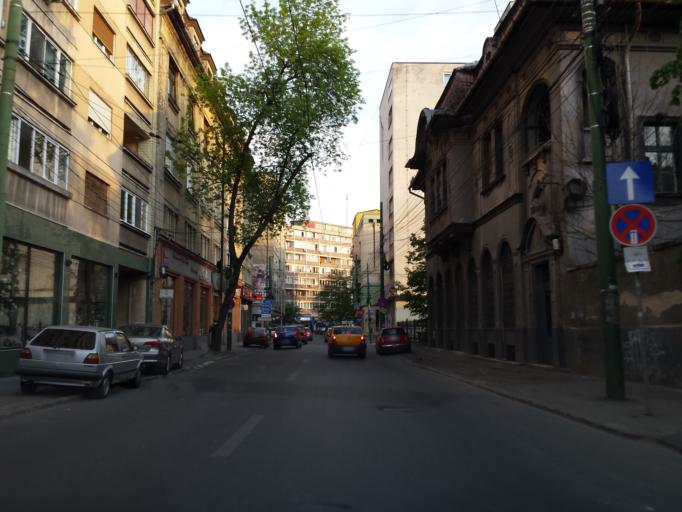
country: RO
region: Timis
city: Timisoara
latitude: 45.7542
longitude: 21.2234
